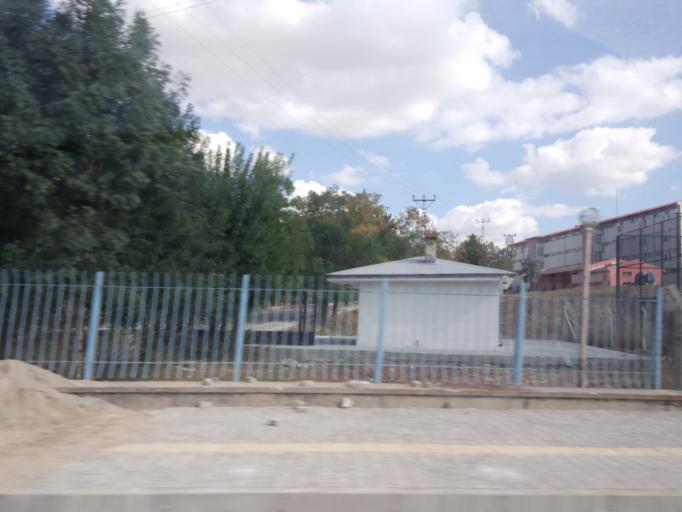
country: TR
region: Tokat
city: Artova
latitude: 40.1107
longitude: 36.3048
